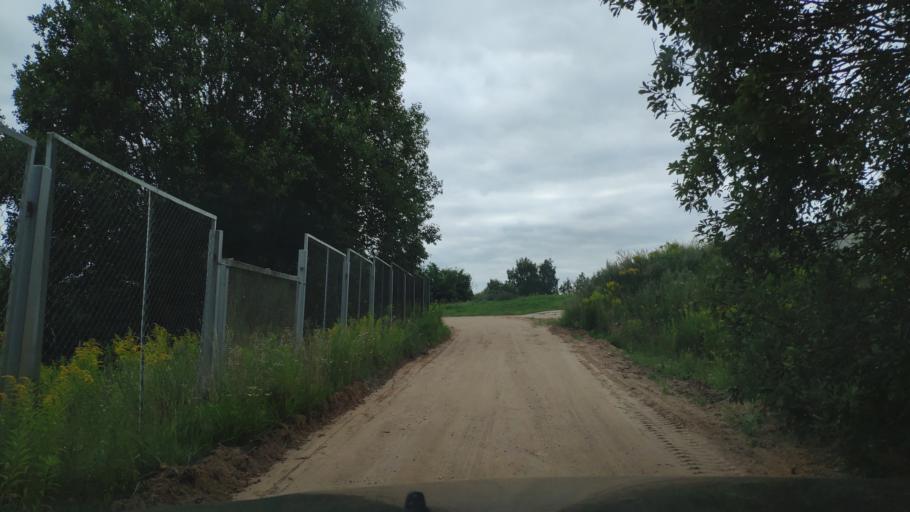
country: BY
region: Minsk
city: Khatsyezhyna
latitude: 53.9324
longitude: 27.2662
